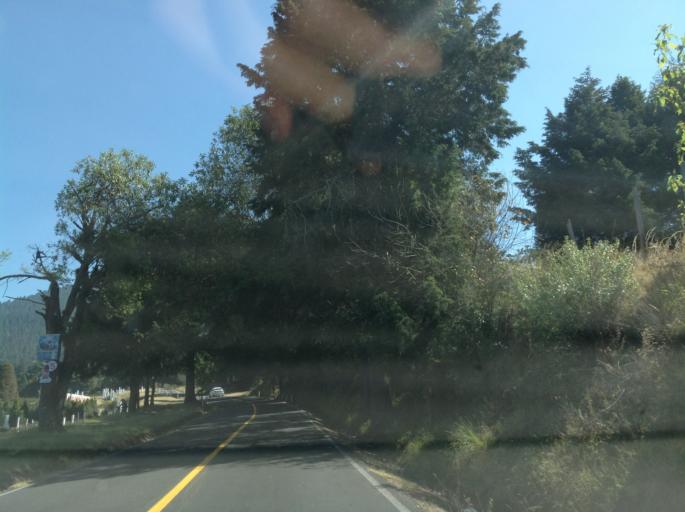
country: MX
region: Mexico
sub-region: Amecameca
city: San Diego Huehuecalco
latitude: 19.0757
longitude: -98.7081
